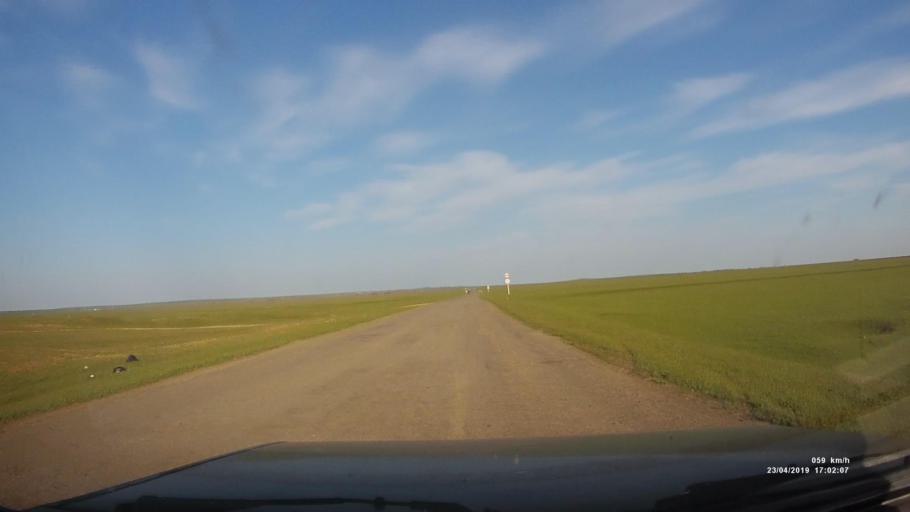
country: RU
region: Kalmykiya
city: Priyutnoye
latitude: 46.2936
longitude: 43.4137
